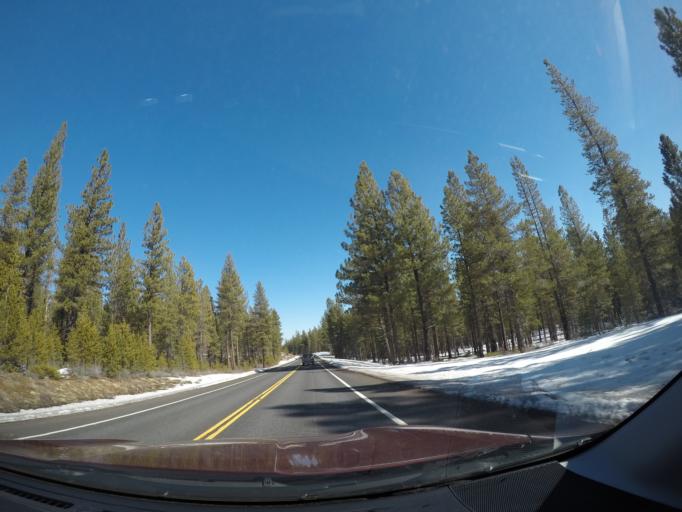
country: US
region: Oregon
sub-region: Deschutes County
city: Three Rivers
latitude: 43.8597
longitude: -121.4956
